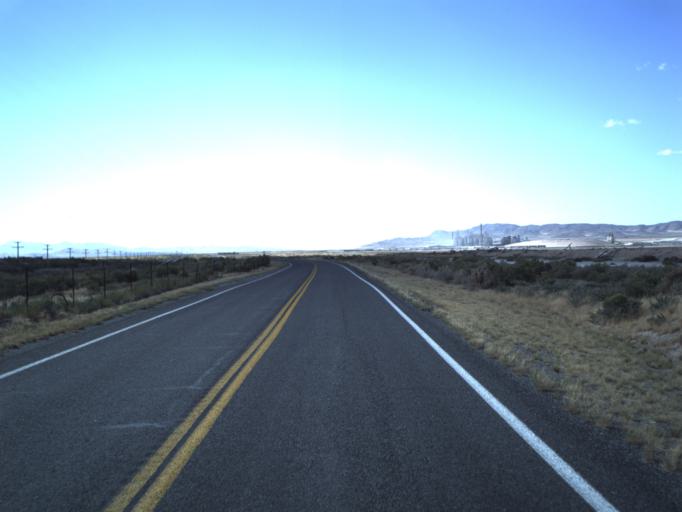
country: US
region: Utah
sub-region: Millard County
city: Delta
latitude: 38.9576
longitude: -112.8044
